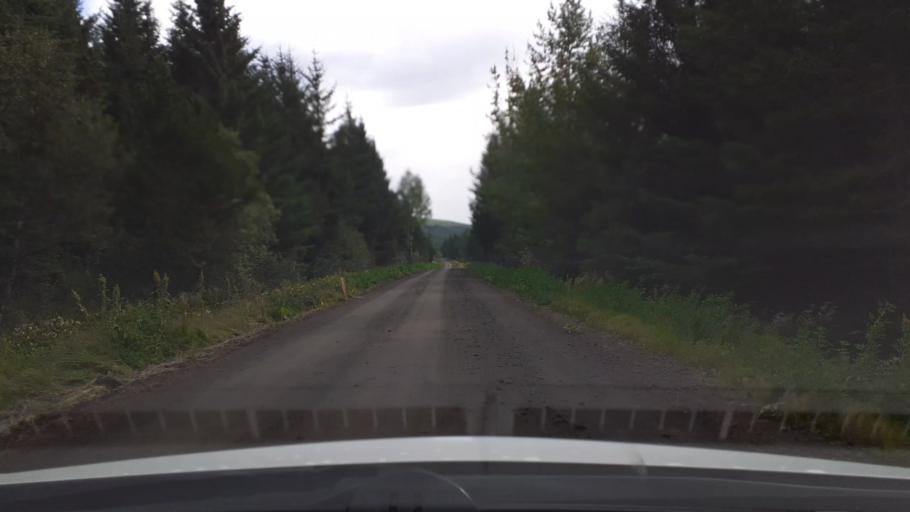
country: IS
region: Capital Region
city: Mosfellsbaer
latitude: 64.5211
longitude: -21.4551
